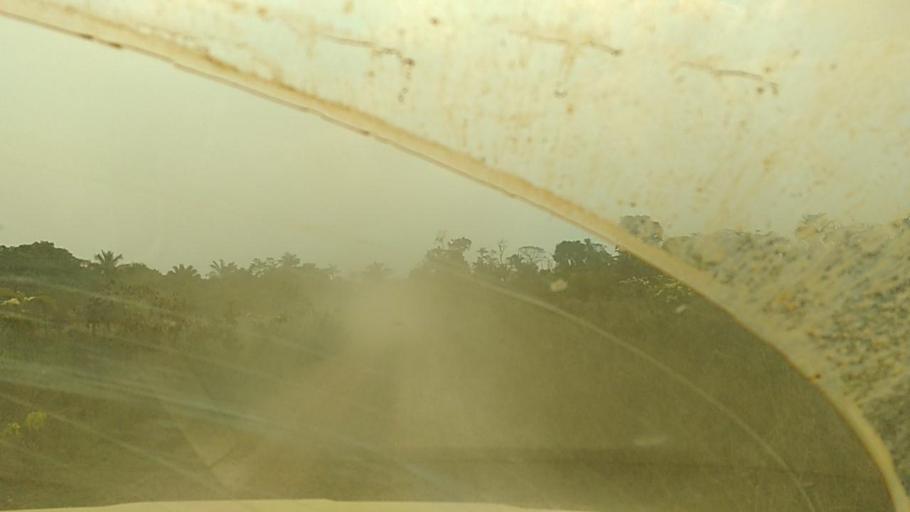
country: BR
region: Rondonia
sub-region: Porto Velho
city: Porto Velho
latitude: -8.7729
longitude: -63.1910
